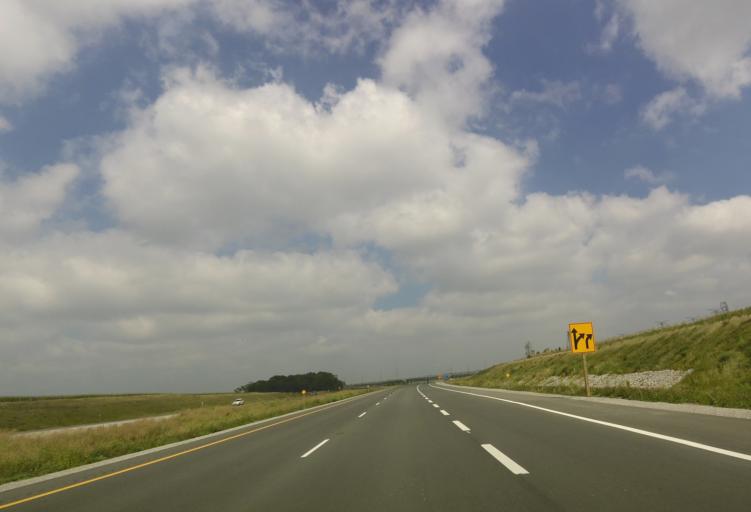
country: CA
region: Ontario
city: Oshawa
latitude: 43.9660
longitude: -78.9152
